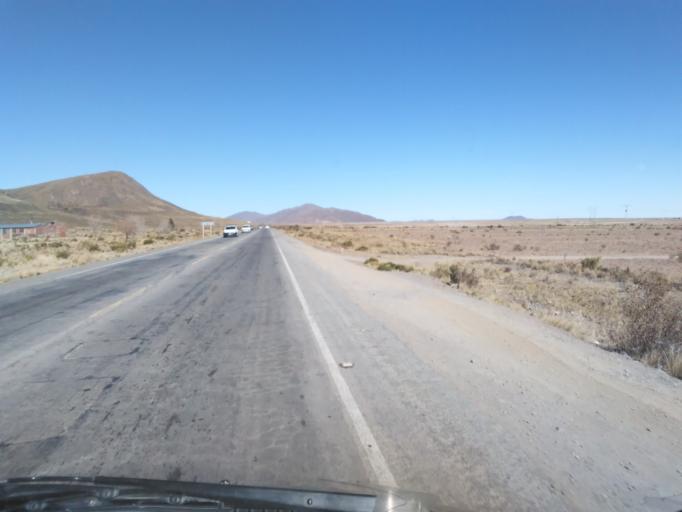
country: BO
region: Oruro
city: Machacamarca
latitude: -18.1052
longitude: -67.0067
